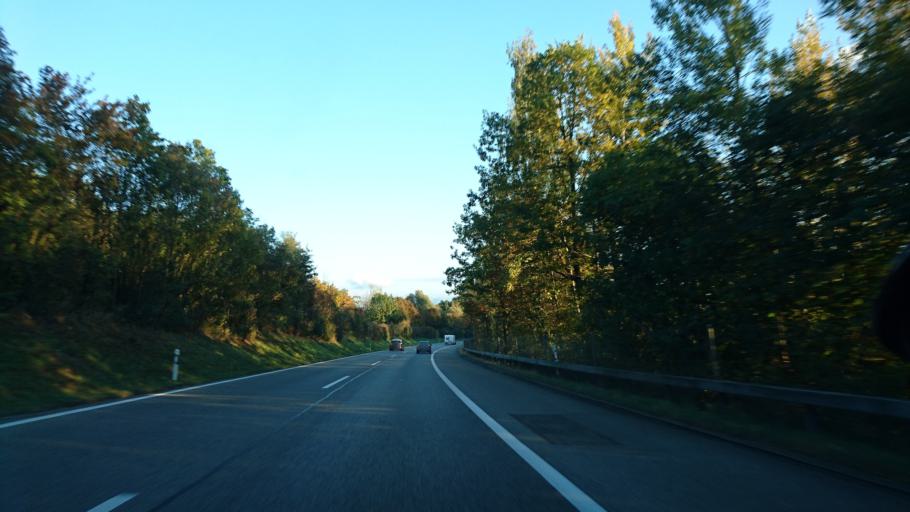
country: CH
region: Bern
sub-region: Bern-Mittelland District
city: Rubigen
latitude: 46.9025
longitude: 7.5301
